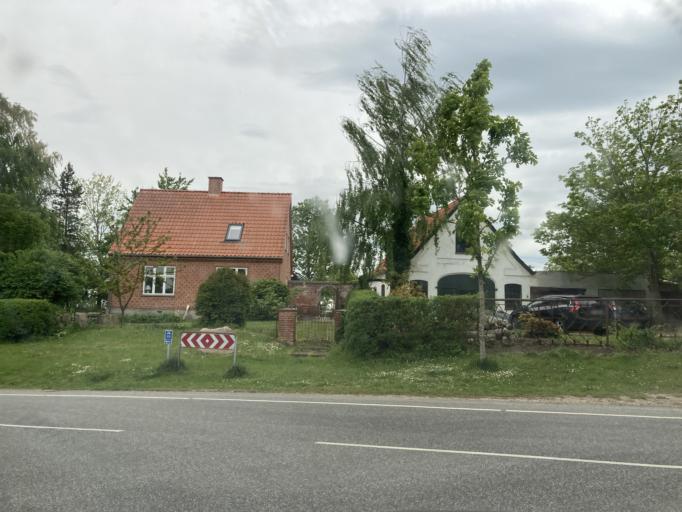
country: DK
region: Zealand
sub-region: Lejre Kommune
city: Lejre
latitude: 55.6353
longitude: 11.9811
